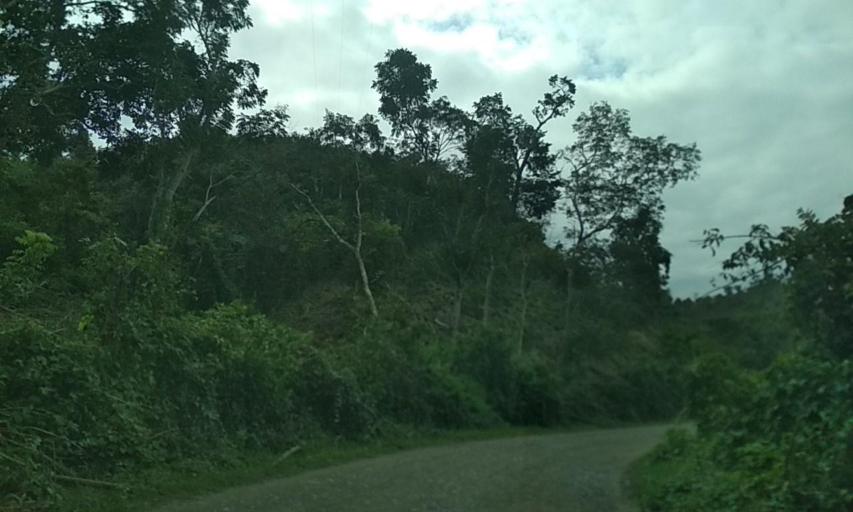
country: MX
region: Veracruz
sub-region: Papantla
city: Residencial Tajin
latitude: 20.6179
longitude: -97.3609
